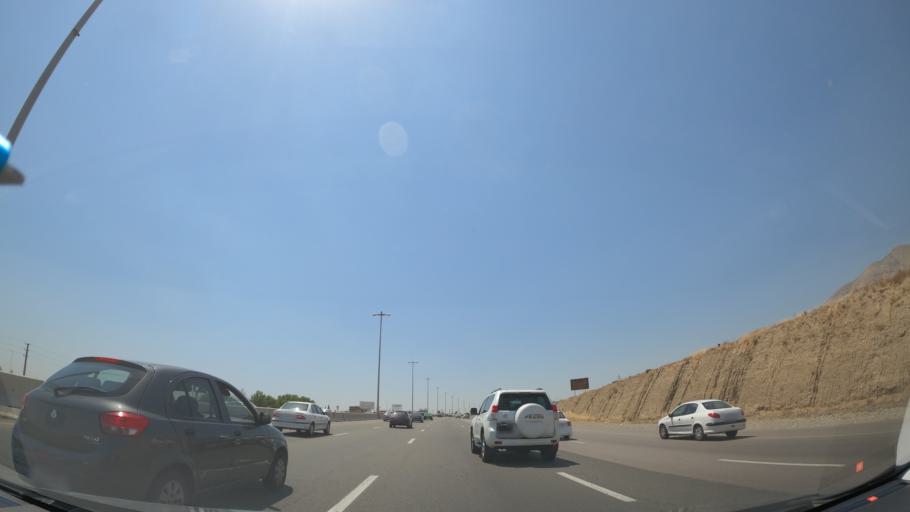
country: IR
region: Tehran
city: Shahr-e Qods
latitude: 35.7449
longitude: 51.0931
